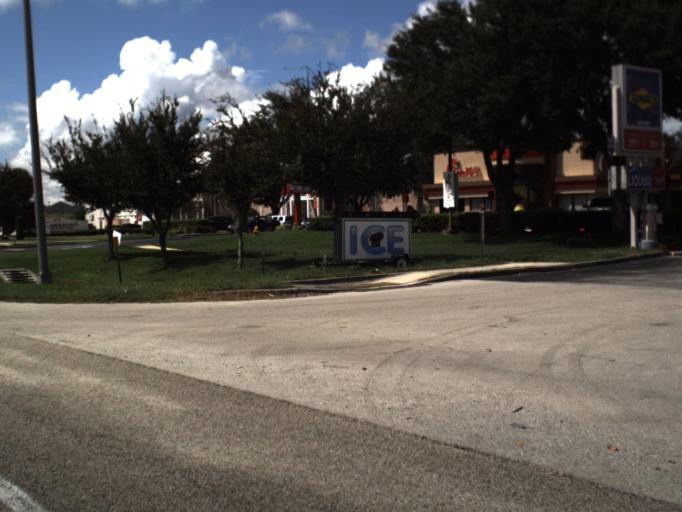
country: US
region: Florida
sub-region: Polk County
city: Medulla
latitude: 27.9818
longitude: -81.9570
